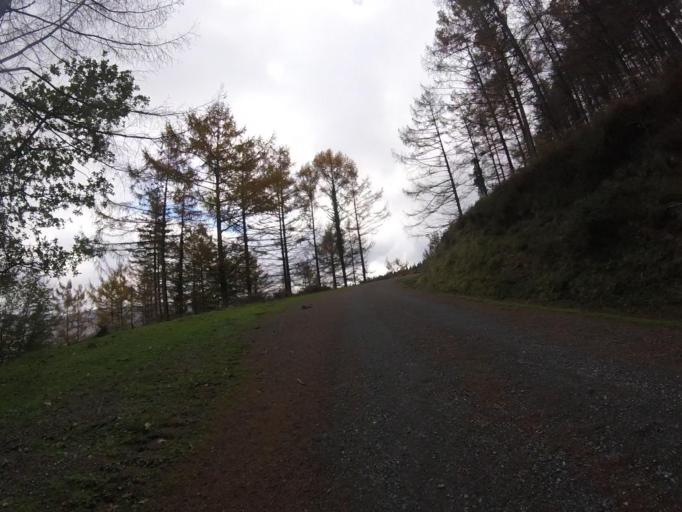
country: ES
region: Navarre
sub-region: Provincia de Navarra
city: Goizueta
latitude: 43.2114
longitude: -1.8244
